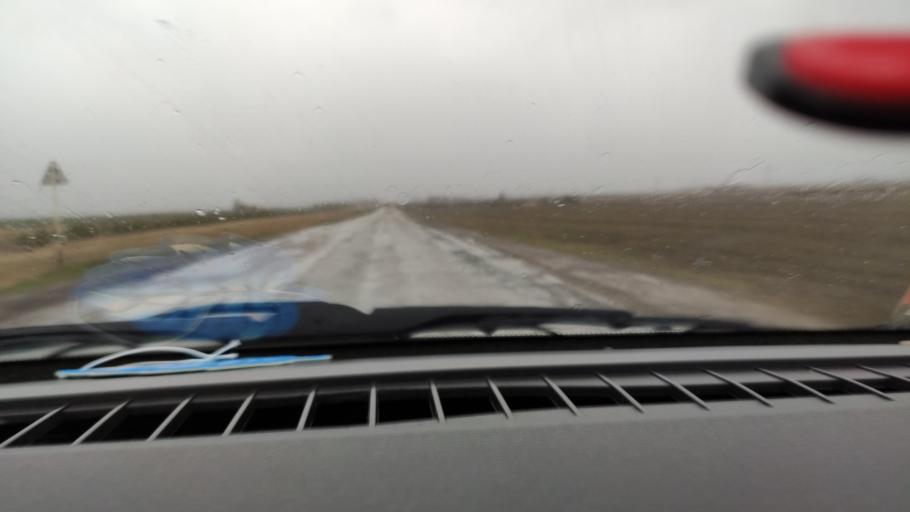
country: RU
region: Tatarstan
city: Cheremshan
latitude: 54.7288
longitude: 51.3177
